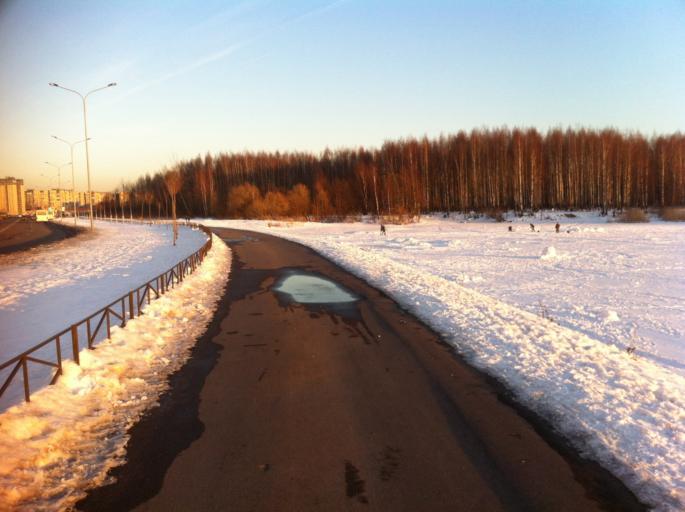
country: RU
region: St.-Petersburg
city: Uritsk
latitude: 59.8578
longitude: 30.1603
